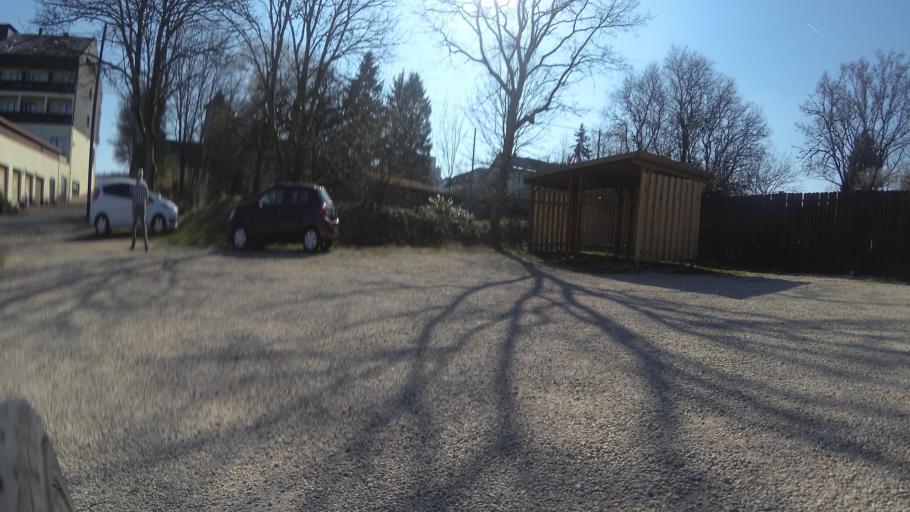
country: DE
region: Rheinland-Pfalz
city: Achtelsbach
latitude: 49.5695
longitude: 7.0591
